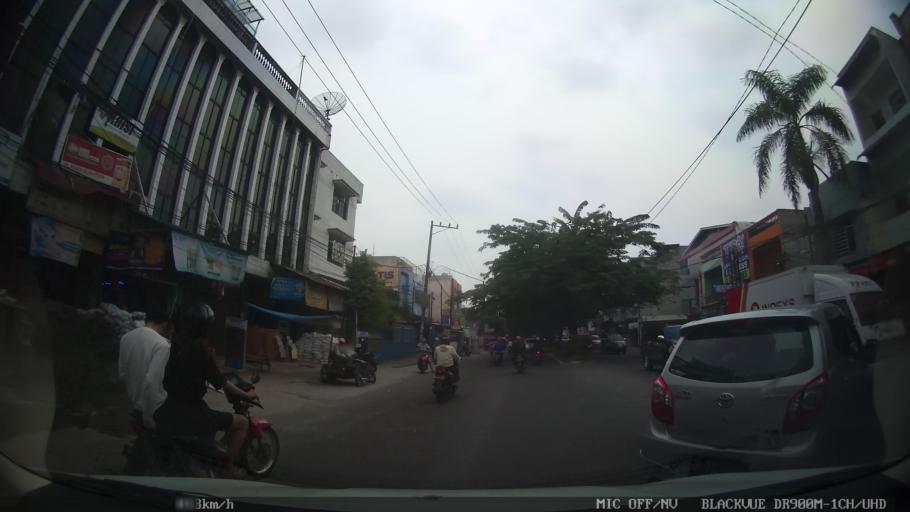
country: ID
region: North Sumatra
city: Medan
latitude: 3.5614
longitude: 98.6895
